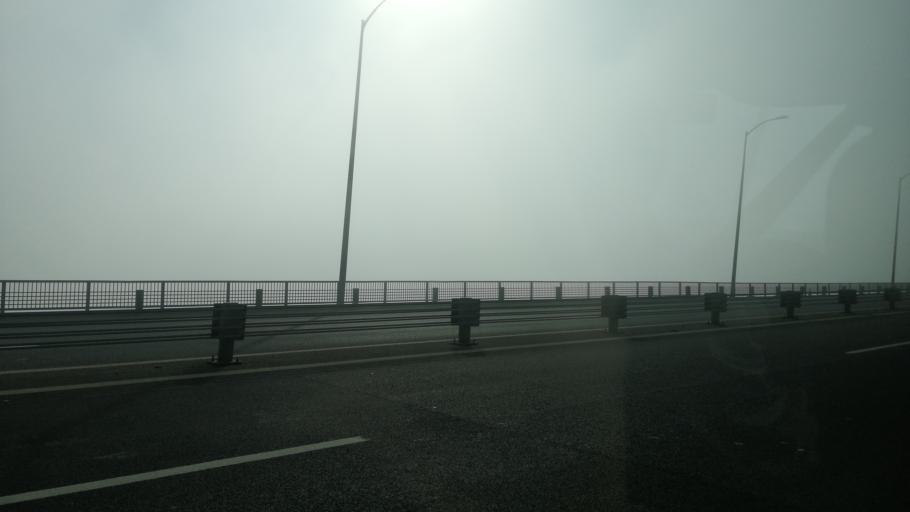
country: TR
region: Kocaeli
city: Tavsanli
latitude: 40.7697
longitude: 29.5181
